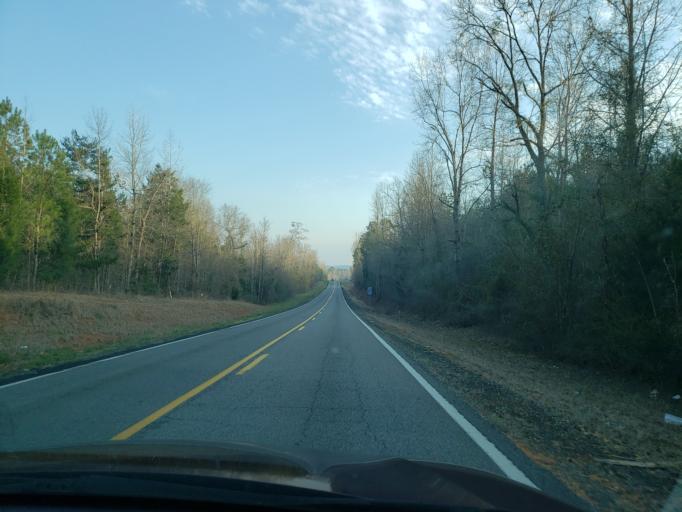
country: US
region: Alabama
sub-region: Hale County
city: Greensboro
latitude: 32.7825
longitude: -87.5883
